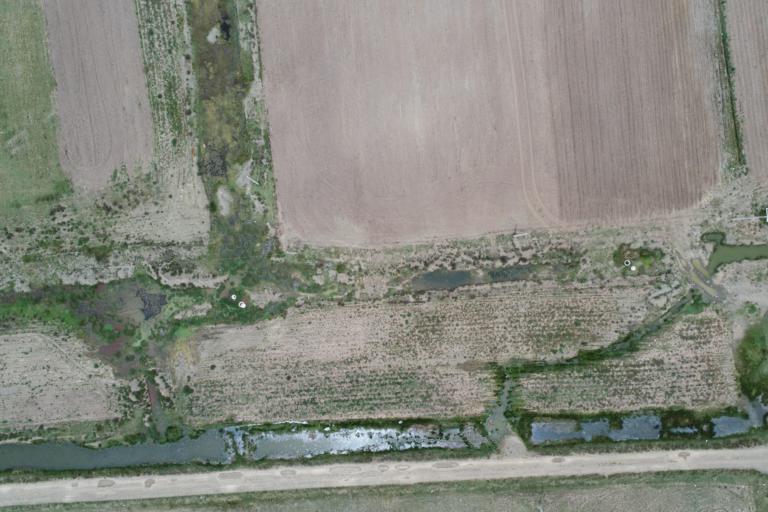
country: BO
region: La Paz
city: La Paz
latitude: -16.5169
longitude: -68.3020
